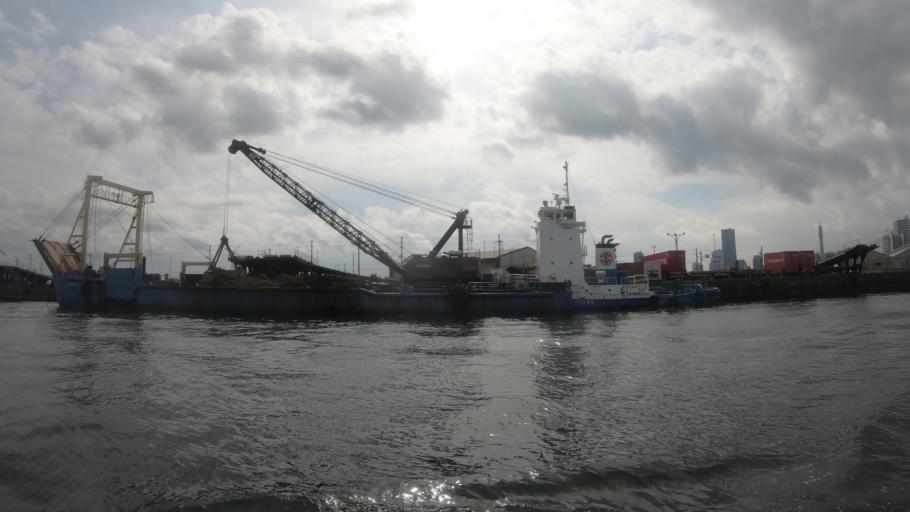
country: JP
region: Kanagawa
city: Yokohama
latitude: 35.4752
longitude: 139.6469
